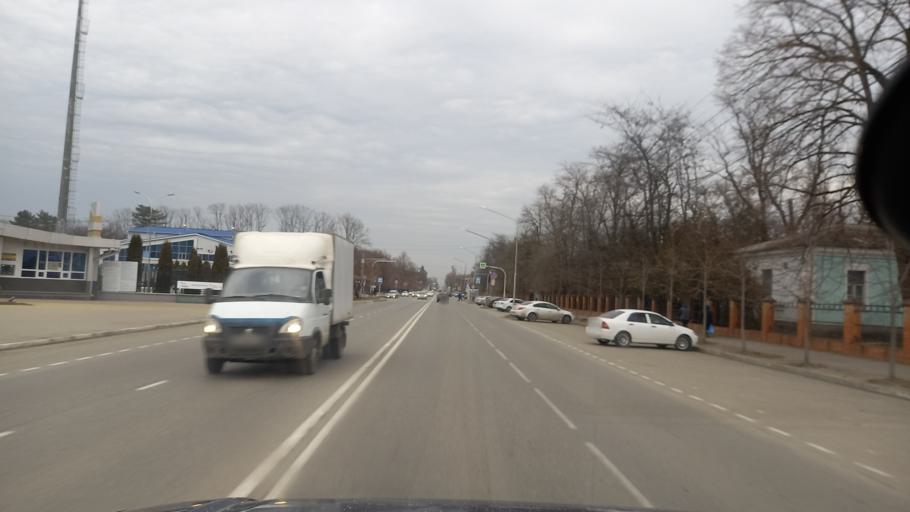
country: RU
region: Adygeya
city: Maykop
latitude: 44.5956
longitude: 40.1090
